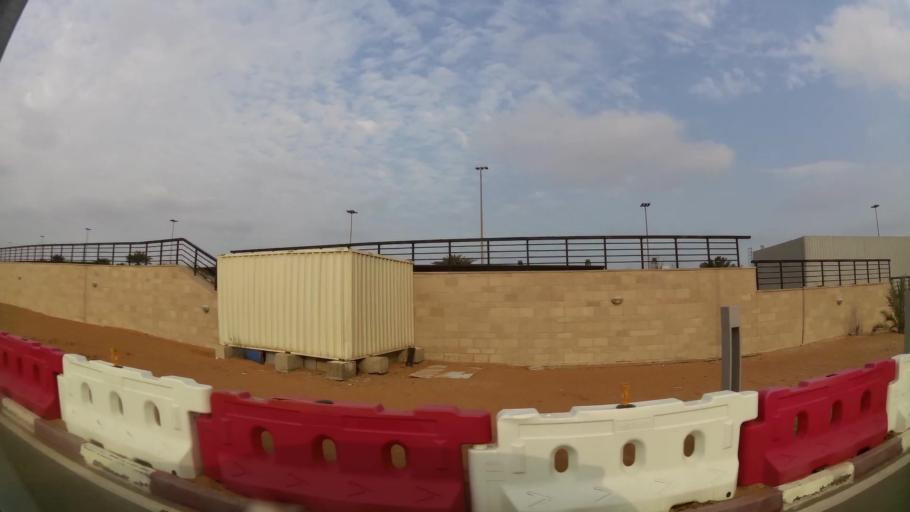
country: AE
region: Abu Dhabi
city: Abu Dhabi
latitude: 24.5032
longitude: 54.3685
